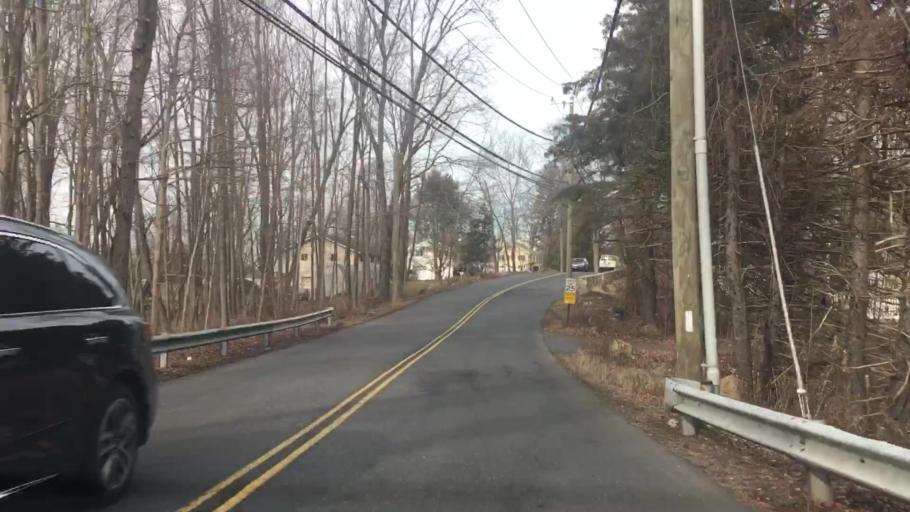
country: US
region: Connecticut
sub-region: Fairfield County
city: Bethel
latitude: 41.4393
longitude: -73.3919
